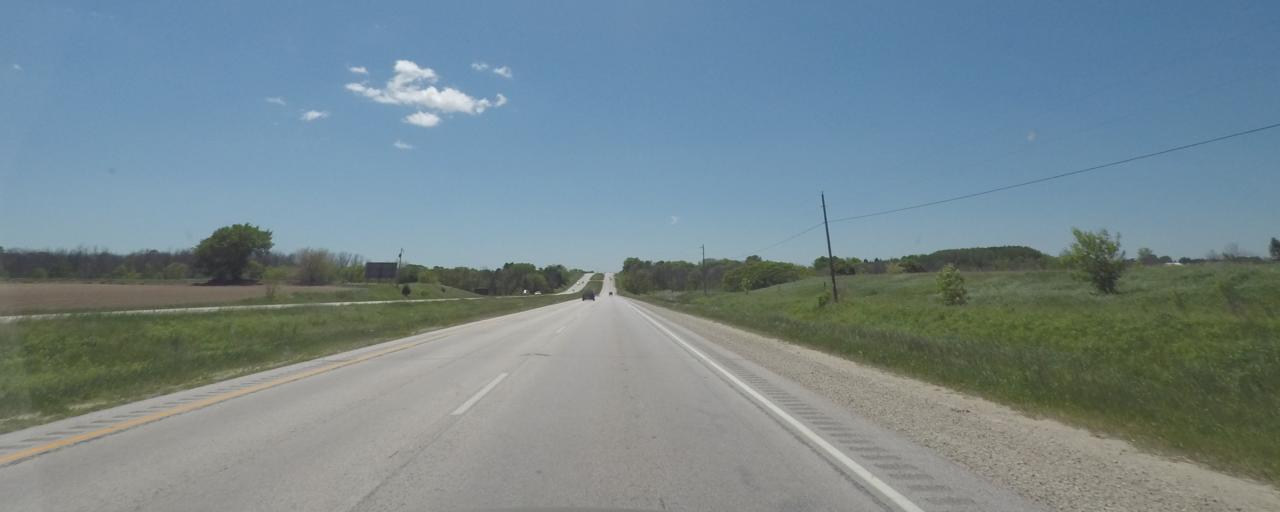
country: US
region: Wisconsin
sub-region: Sheboygan County
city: Plymouth
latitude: 43.7269
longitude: -87.9412
